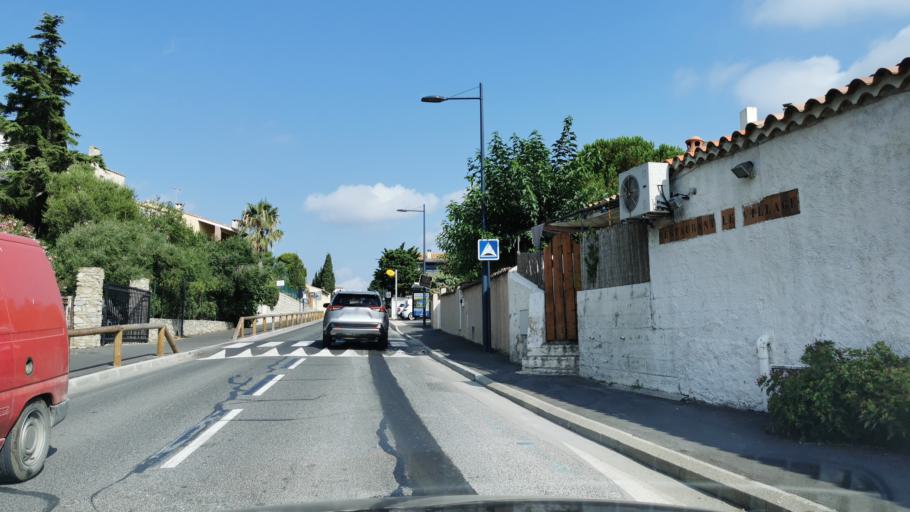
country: FR
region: Languedoc-Roussillon
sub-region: Departement de l'Aude
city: Leucate
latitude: 42.9074
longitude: 3.0326
